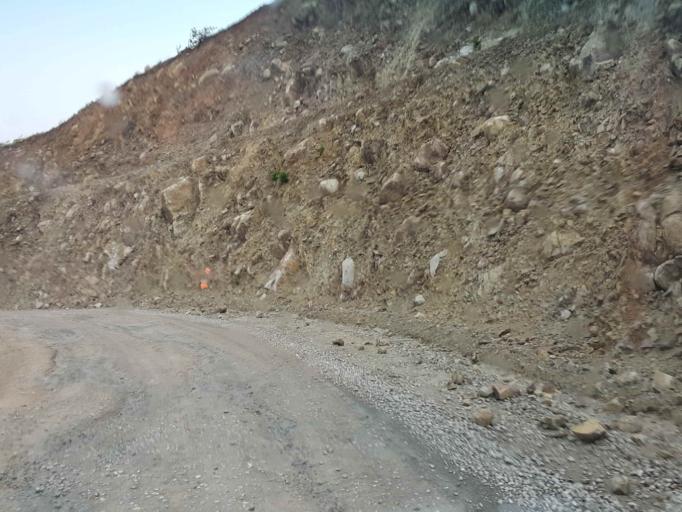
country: CR
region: Guanacaste
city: Juntas
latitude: 10.2643
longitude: -84.8356
